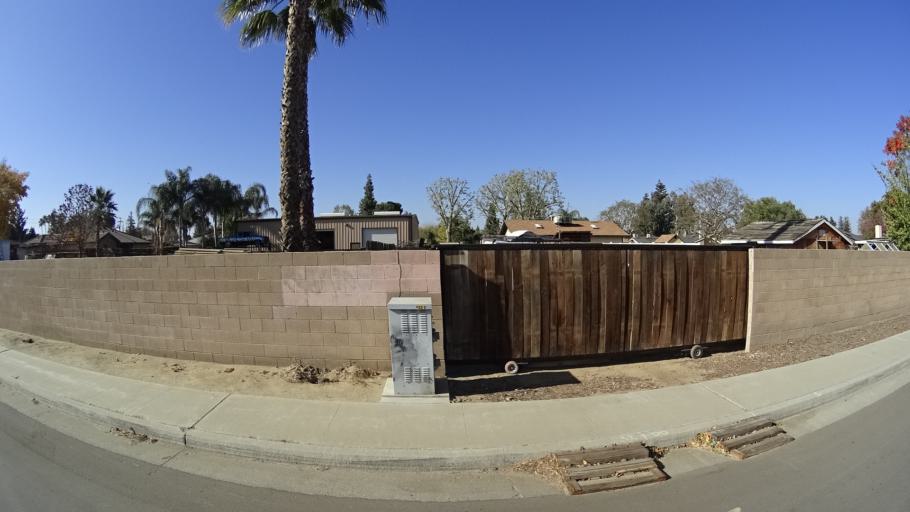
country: US
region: California
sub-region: Kern County
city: Rosedale
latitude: 35.3769
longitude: -119.1281
